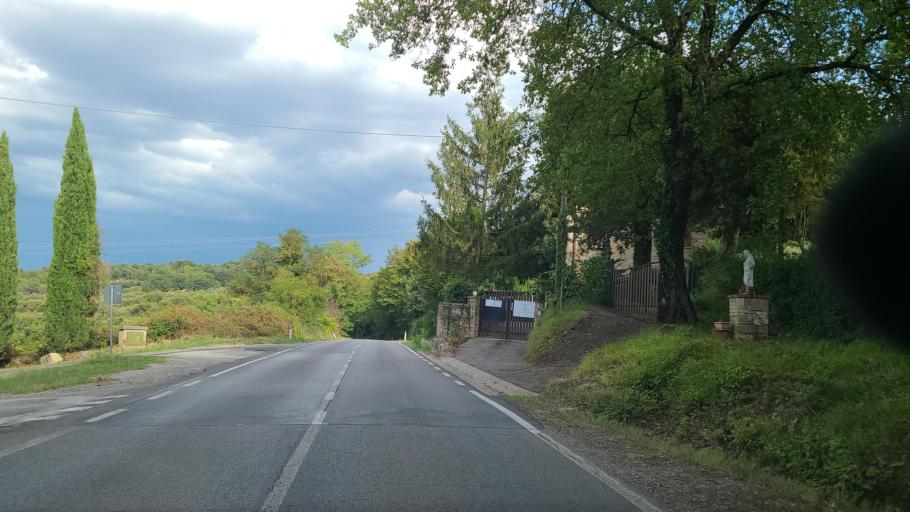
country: IT
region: Tuscany
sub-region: Provincia di Siena
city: San Gimignano
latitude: 43.4867
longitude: 10.9929
